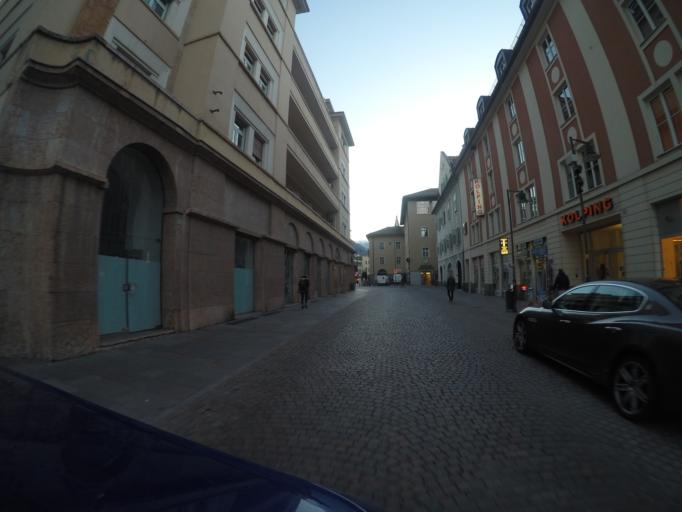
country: IT
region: Trentino-Alto Adige
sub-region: Bolzano
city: Bolzano
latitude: 46.4976
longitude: 11.3504
